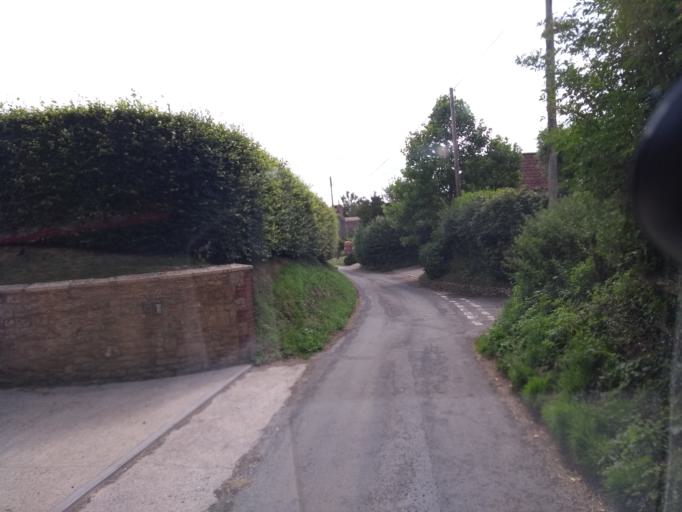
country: GB
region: England
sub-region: Somerset
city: Ilminster
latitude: 50.9159
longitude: -2.8667
